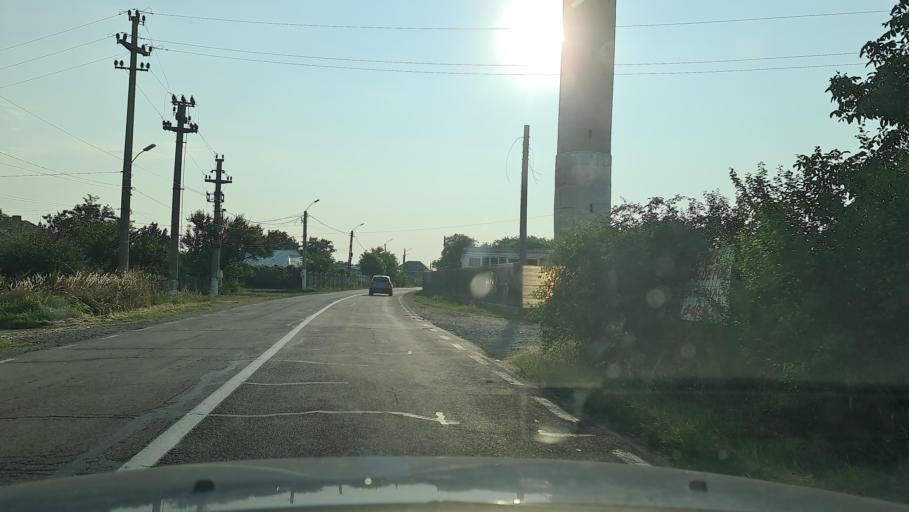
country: RO
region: Calarasi
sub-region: Comuna Dor Marunt
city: Dor Marunt
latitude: 44.4365
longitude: 26.9572
